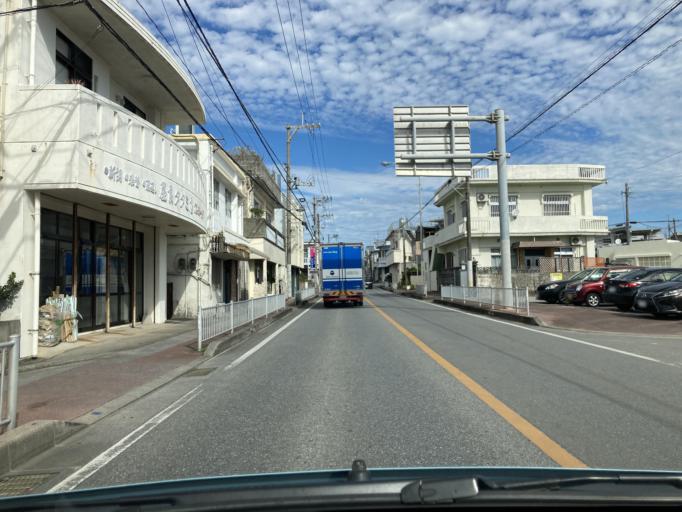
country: JP
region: Okinawa
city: Ishikawa
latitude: 26.4103
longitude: 127.7323
